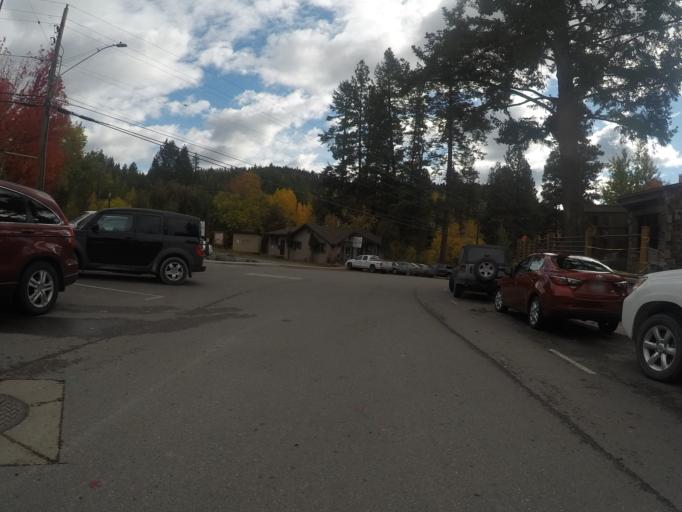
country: US
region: Montana
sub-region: Flathead County
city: Bigfork
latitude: 48.0610
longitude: -114.0728
